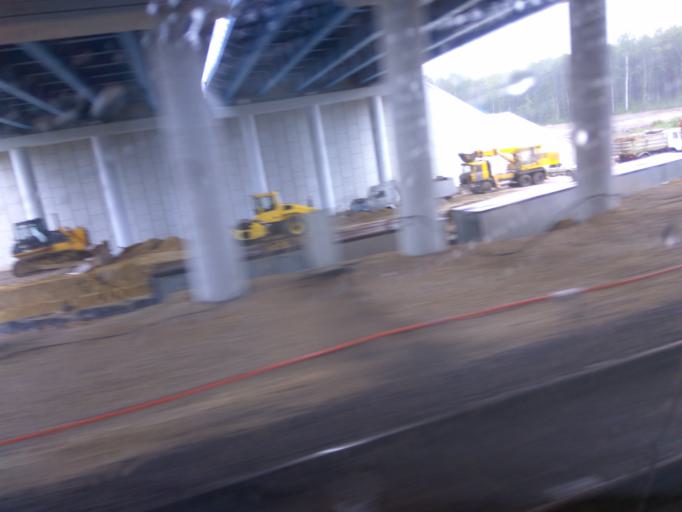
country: RU
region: Moskovskaya
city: Zhilevo
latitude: 54.9945
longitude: 38.0268
